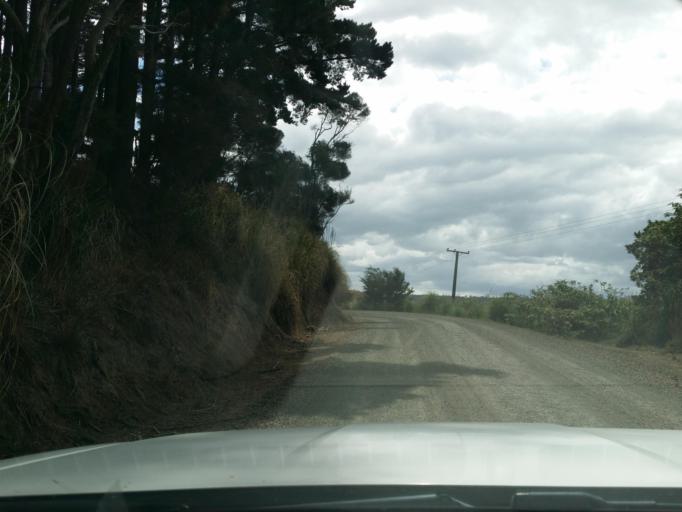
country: NZ
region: Auckland
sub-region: Auckland
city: Wellsford
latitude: -36.3043
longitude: 174.1166
